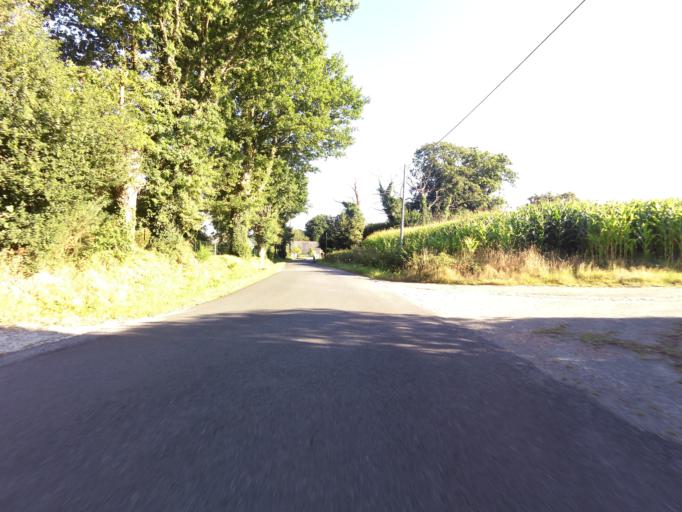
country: FR
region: Brittany
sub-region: Departement du Morbihan
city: Pluherlin
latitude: 47.7169
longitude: -2.3558
